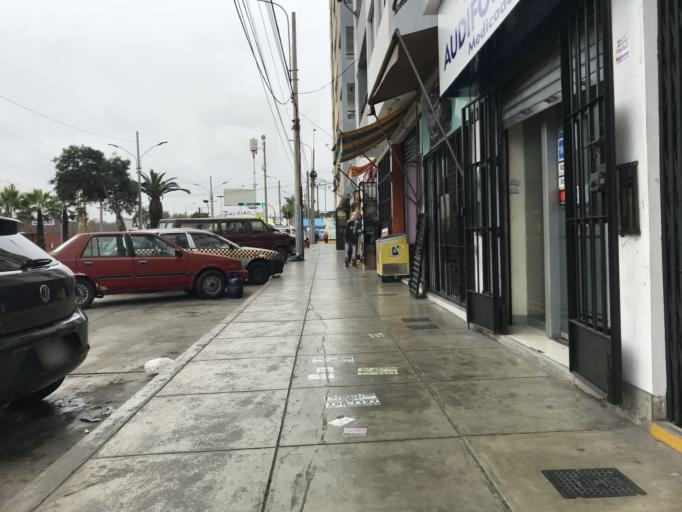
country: PE
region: Callao
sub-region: Callao
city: Callao
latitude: -12.0744
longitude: -77.0872
